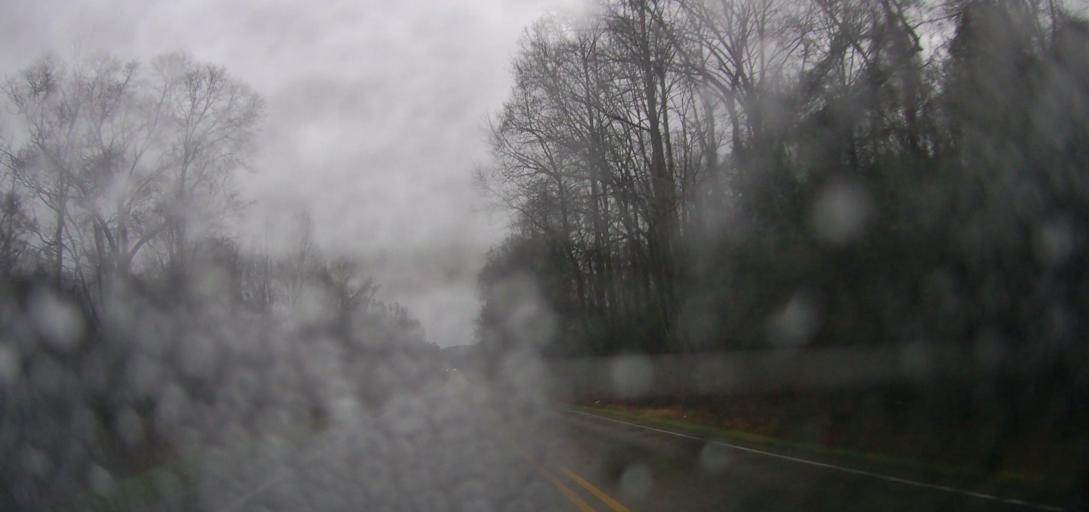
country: US
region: Alabama
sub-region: Autauga County
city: Prattville
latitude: 32.5108
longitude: -86.5879
